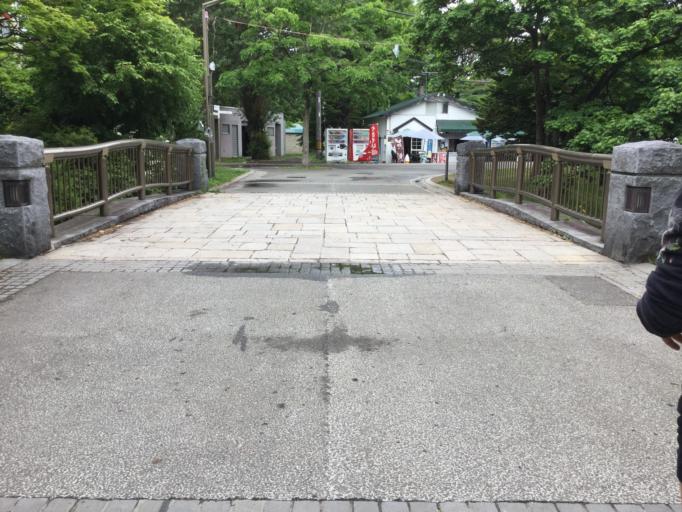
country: JP
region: Hokkaido
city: Sapporo
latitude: 43.0469
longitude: 141.3541
